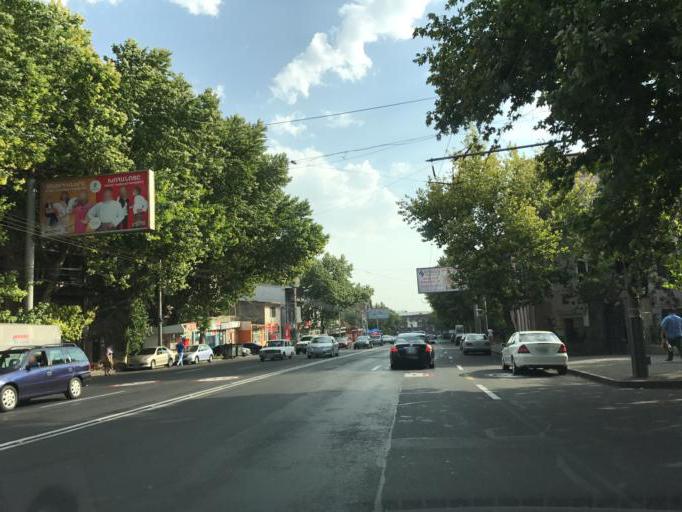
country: AM
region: Yerevan
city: Yerevan
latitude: 40.1895
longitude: 44.5283
